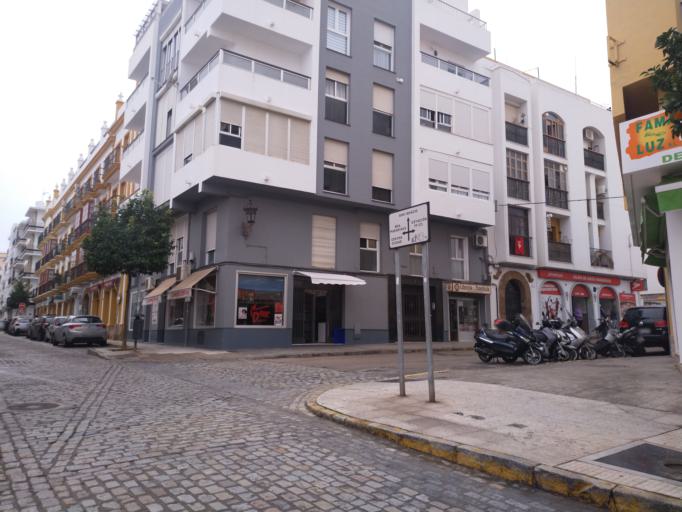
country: ES
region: Andalusia
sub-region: Provincia de Cadiz
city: San Fernando
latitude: 36.4706
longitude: -6.1968
